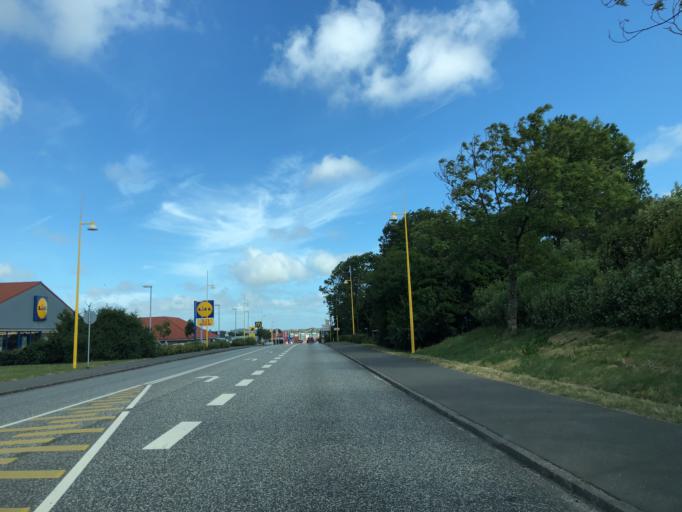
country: DK
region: Central Jutland
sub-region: Struer Kommune
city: Struer
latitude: 56.4859
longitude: 8.5836
